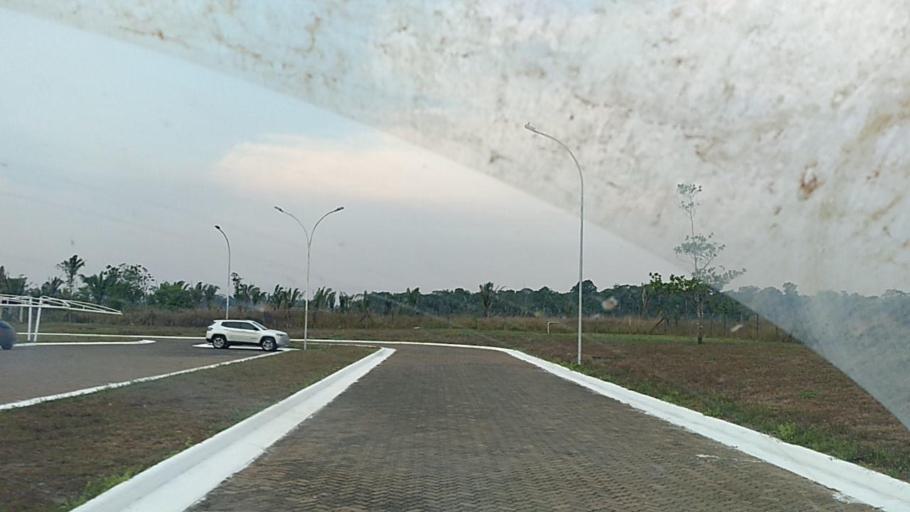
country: BR
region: Rondonia
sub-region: Porto Velho
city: Porto Velho
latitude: -8.7113
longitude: -63.8962
